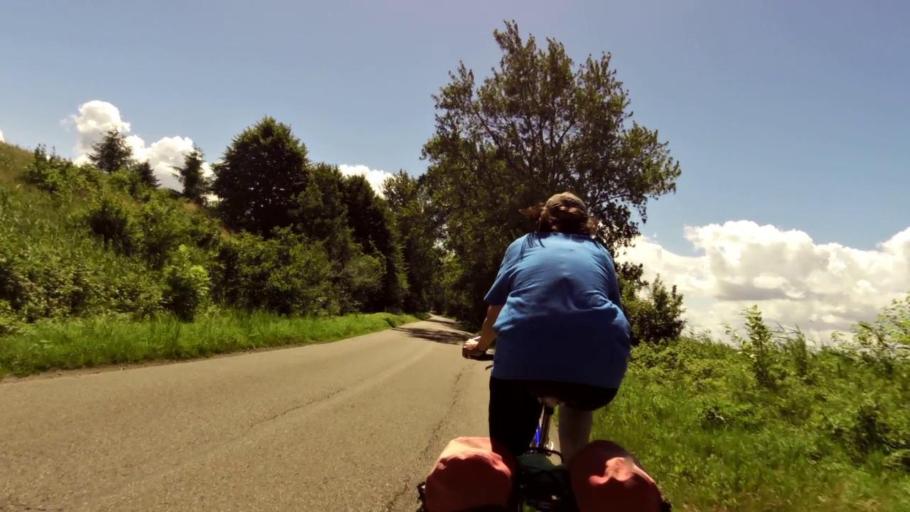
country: PL
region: West Pomeranian Voivodeship
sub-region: Koszalin
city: Koszalin
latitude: 54.2862
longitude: 16.2094
